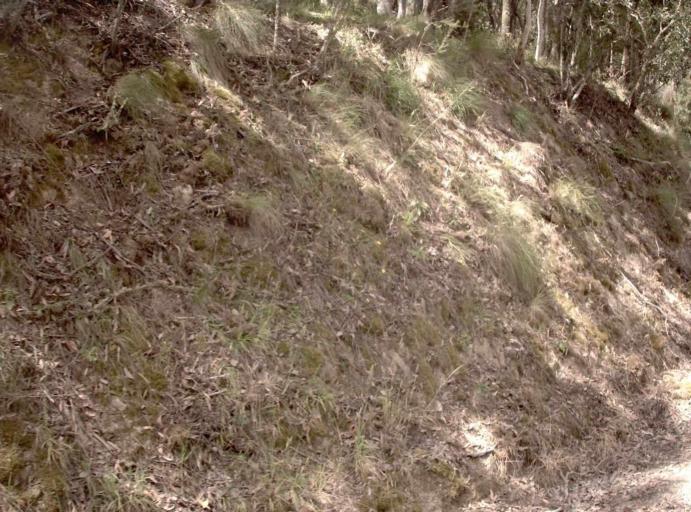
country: AU
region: New South Wales
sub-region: Bombala
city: Bombala
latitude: -37.1745
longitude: 148.6949
